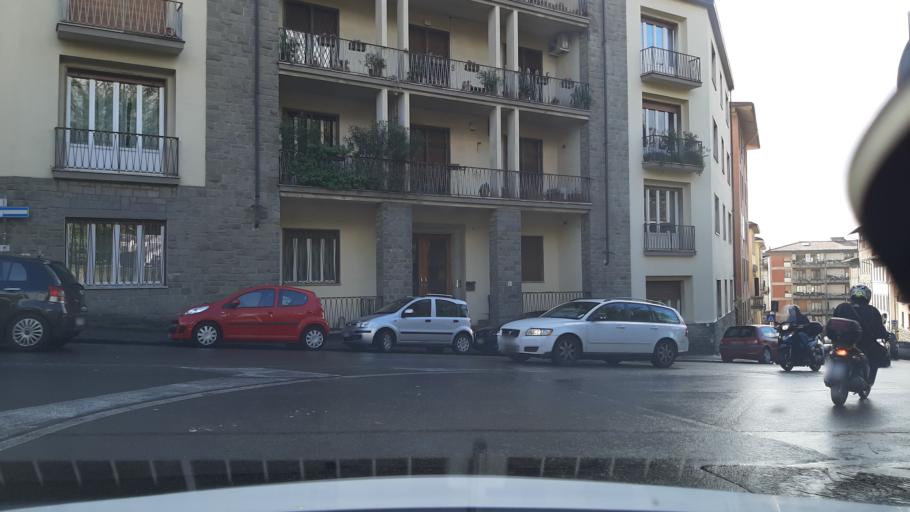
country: IT
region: Tuscany
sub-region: Province of Florence
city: Florence
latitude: 43.7897
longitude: 11.2587
